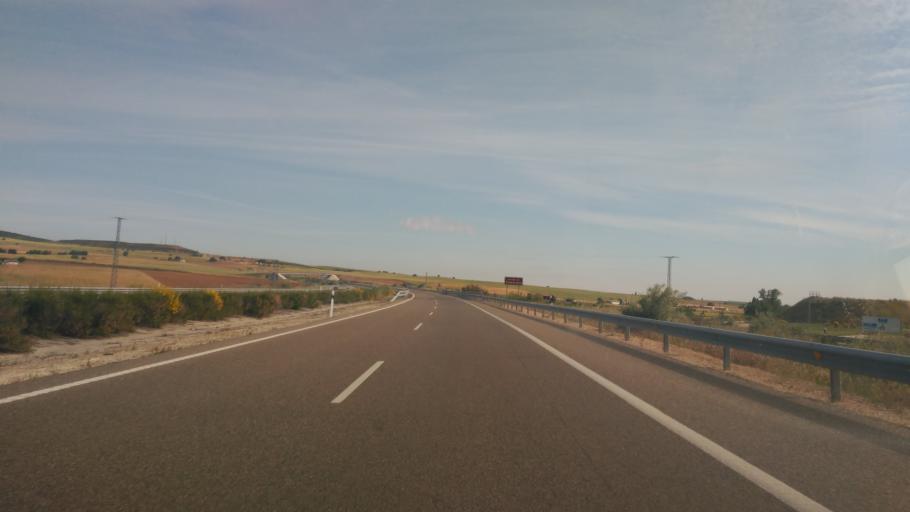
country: ES
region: Castille and Leon
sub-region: Provincia de Zamora
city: Corrales
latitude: 41.3573
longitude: -5.7132
